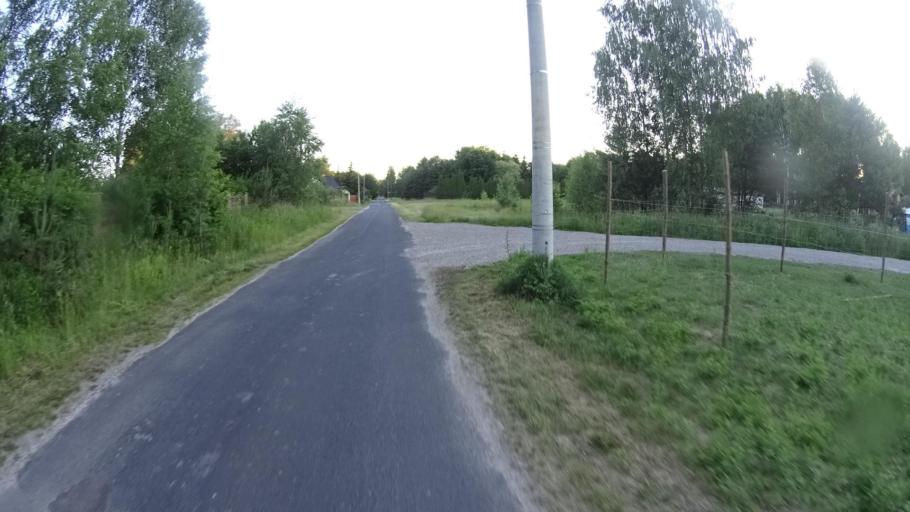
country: PL
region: Masovian Voivodeship
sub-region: Powiat warszawski zachodni
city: Truskaw
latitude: 52.2766
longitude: 20.7053
